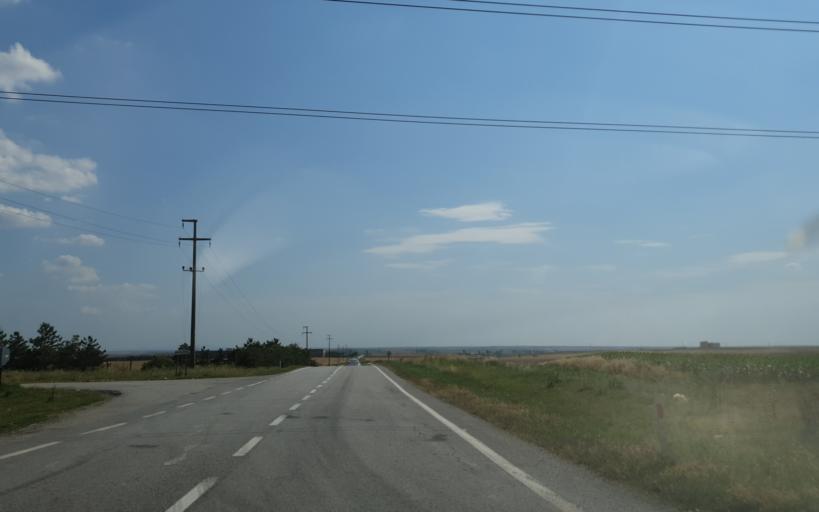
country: TR
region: Kirklareli
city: Buyukkaristiran
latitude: 41.3278
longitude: 27.5289
